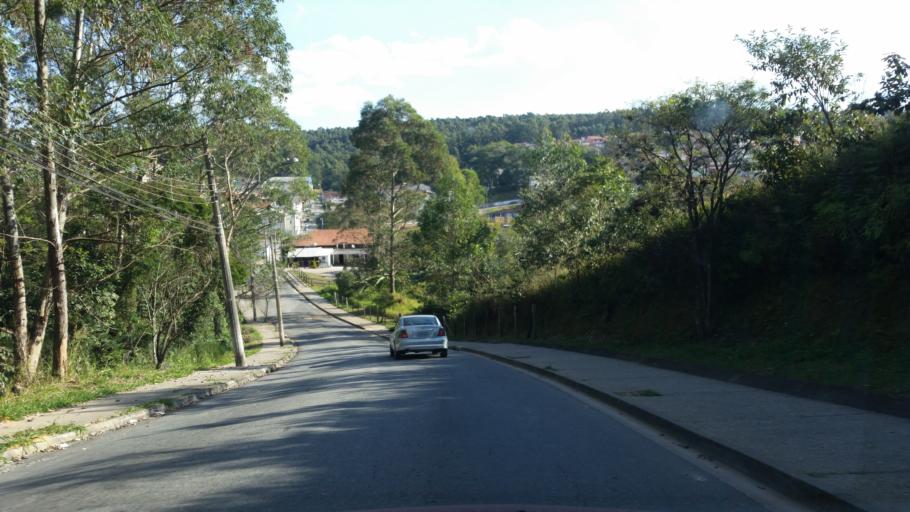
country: BR
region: Sao Paulo
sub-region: Mairinque
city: Mairinque
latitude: -23.5162
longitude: -47.2545
